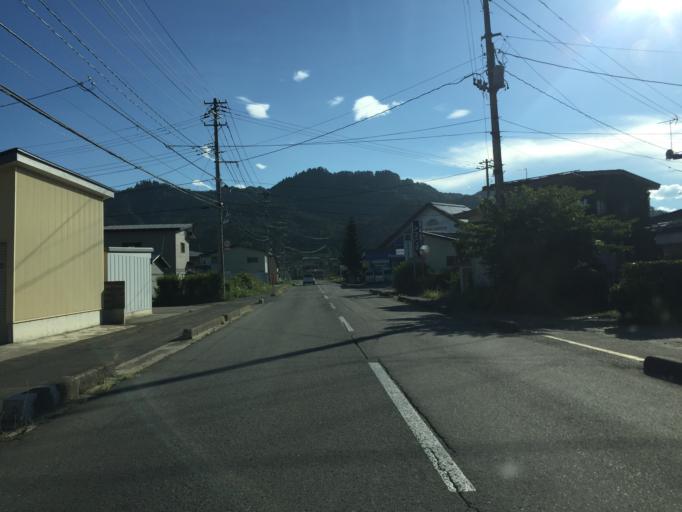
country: JP
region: Yamagata
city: Yonezawa
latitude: 37.9107
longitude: 140.0873
